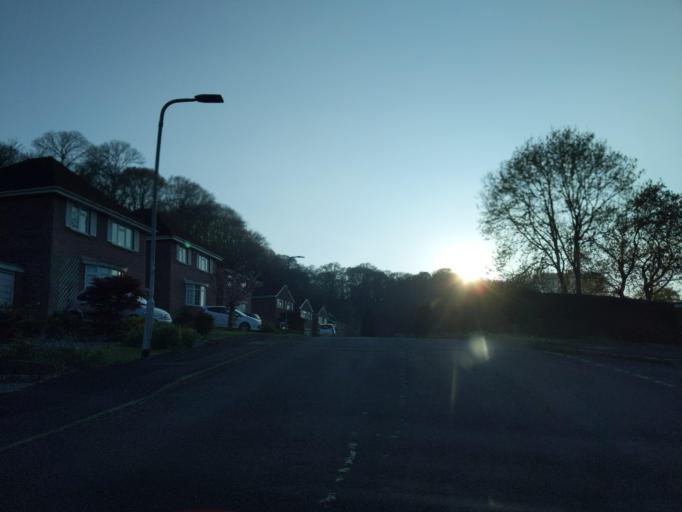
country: GB
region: England
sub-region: Plymouth
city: Plymstock
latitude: 50.3489
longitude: -4.0897
